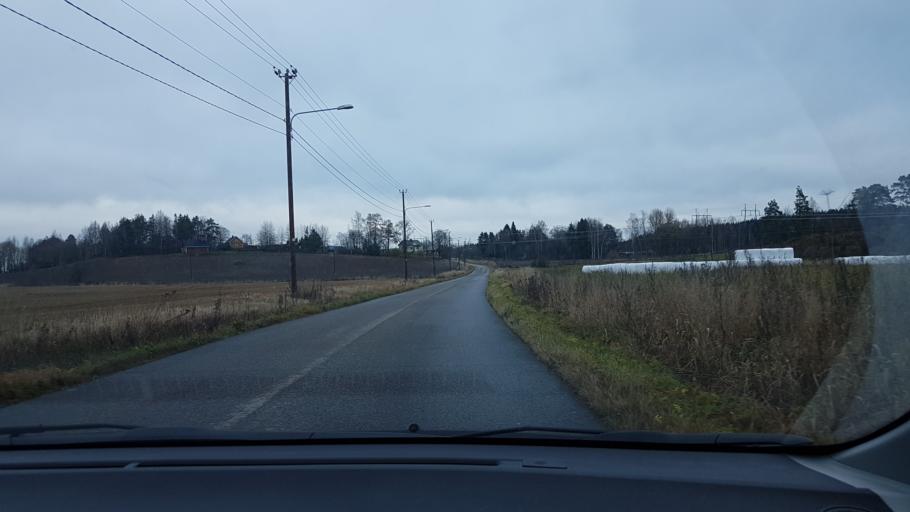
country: FI
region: Uusimaa
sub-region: Helsinki
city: Vantaa
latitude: 60.2793
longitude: 25.1365
